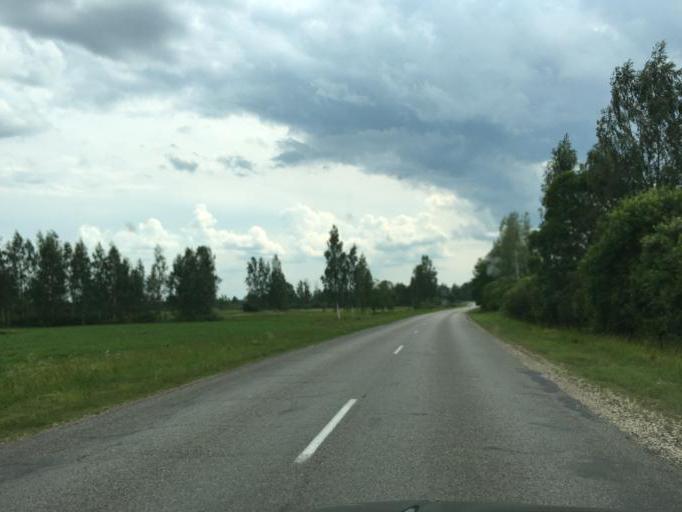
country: LV
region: Rugaju
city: Rugaji
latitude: 56.9422
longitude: 27.0682
